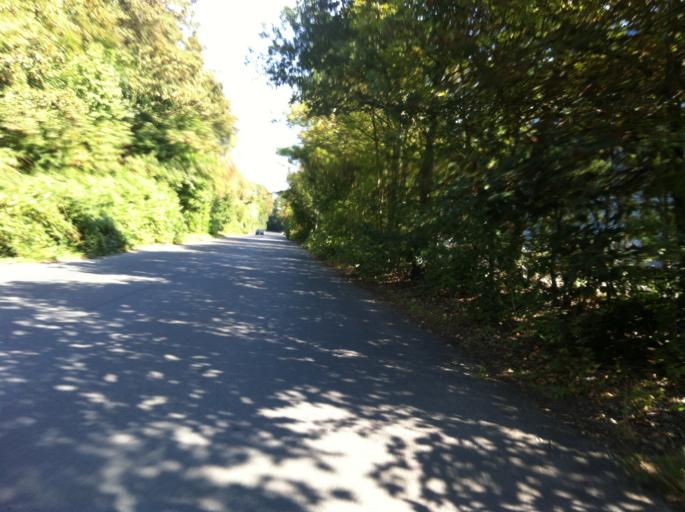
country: DE
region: North Rhine-Westphalia
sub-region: Regierungsbezirk Koln
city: Hoehenberg
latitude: 50.9140
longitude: 7.0220
